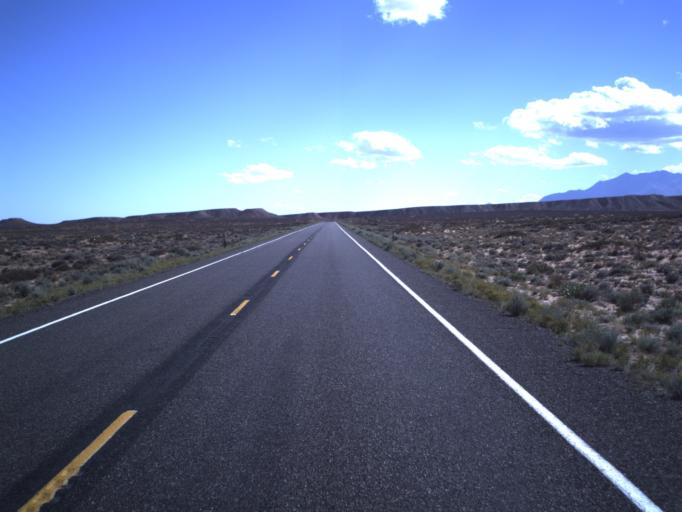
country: US
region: Utah
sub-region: Wayne County
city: Loa
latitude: 38.1715
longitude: -110.6242
